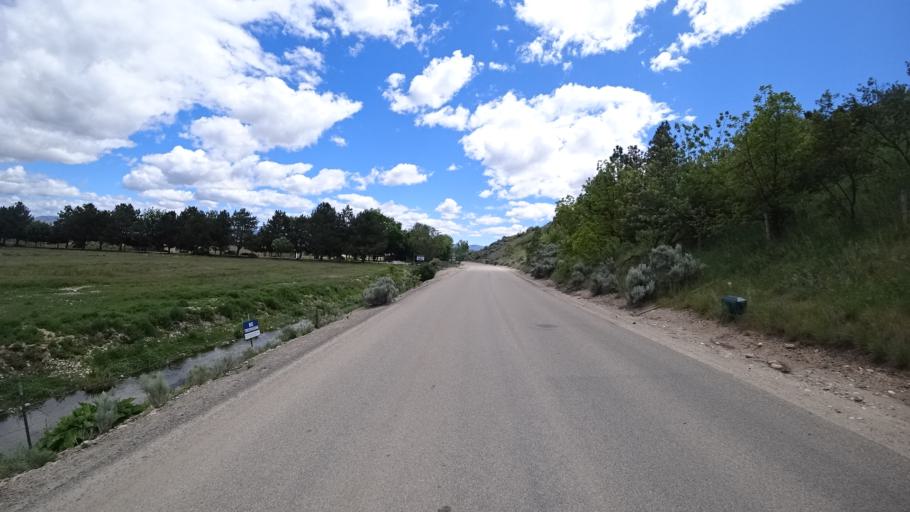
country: US
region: Idaho
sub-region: Ada County
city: Eagle
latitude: 43.6638
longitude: -116.3309
